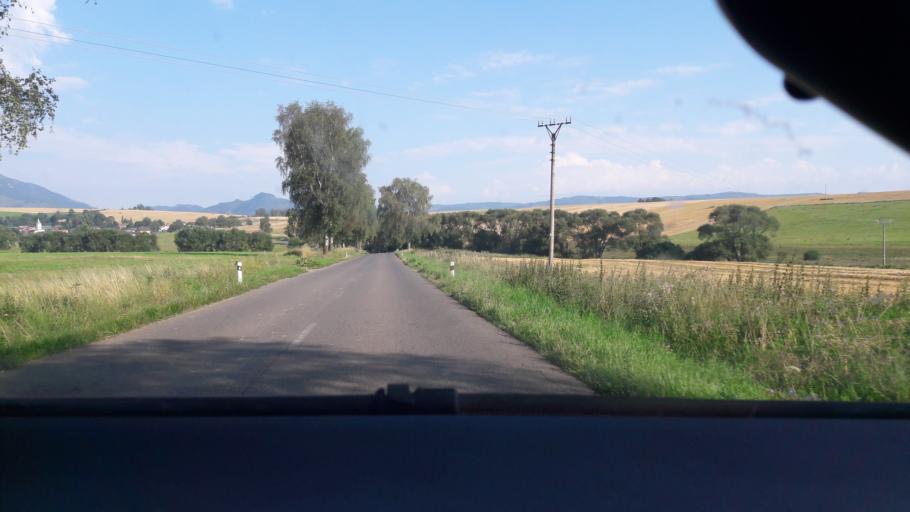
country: SK
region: Presovsky
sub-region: Okres Presov
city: Kezmarok
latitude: 49.1816
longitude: 20.3987
